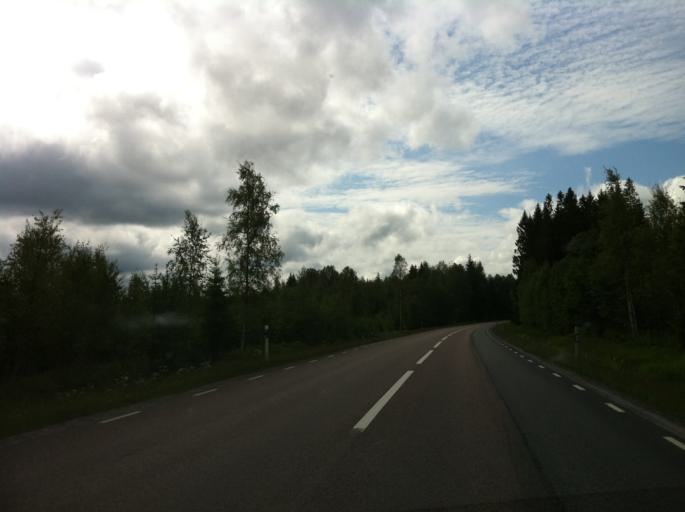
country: SE
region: Vaermland
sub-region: Sunne Kommun
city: Sunne
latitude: 59.7089
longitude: 13.1479
